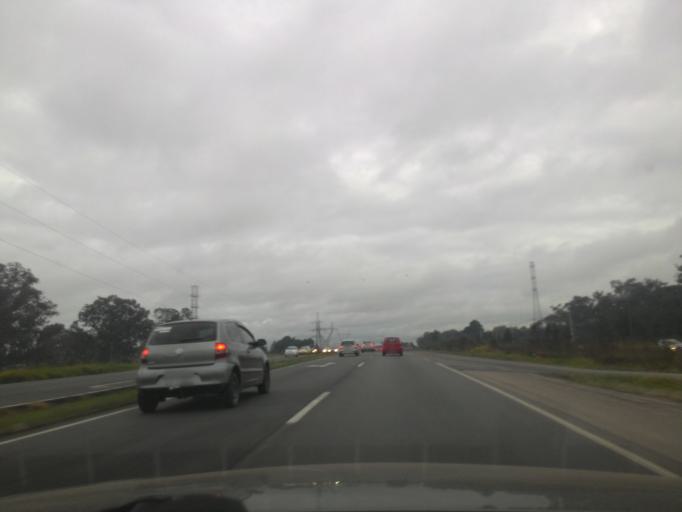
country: BR
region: Parana
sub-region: Araucaria
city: Araucaria
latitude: -25.5489
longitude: -49.3241
